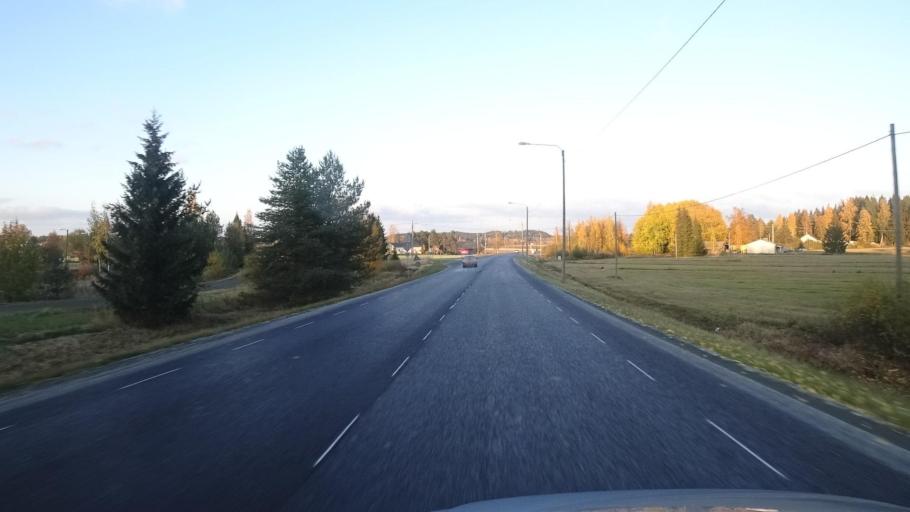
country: FI
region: Haeme
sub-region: Forssa
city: Jokioinen
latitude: 60.8190
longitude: 23.5484
